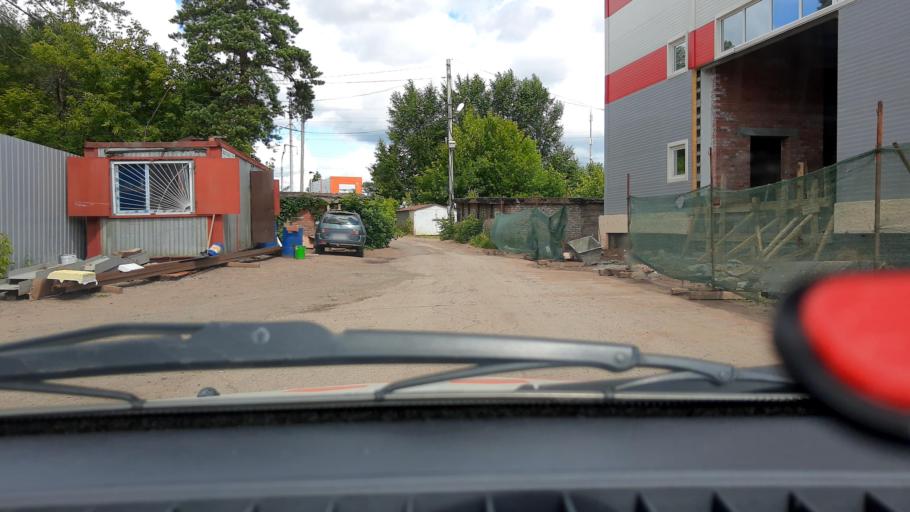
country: RU
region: Bashkortostan
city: Avdon
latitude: 54.6904
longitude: 55.8196
